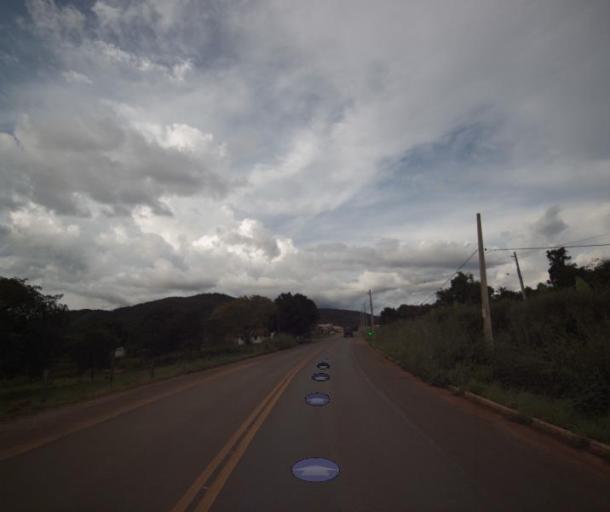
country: BR
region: Goias
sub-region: Niquelandia
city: Niquelandia
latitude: -14.4709
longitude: -48.4879
